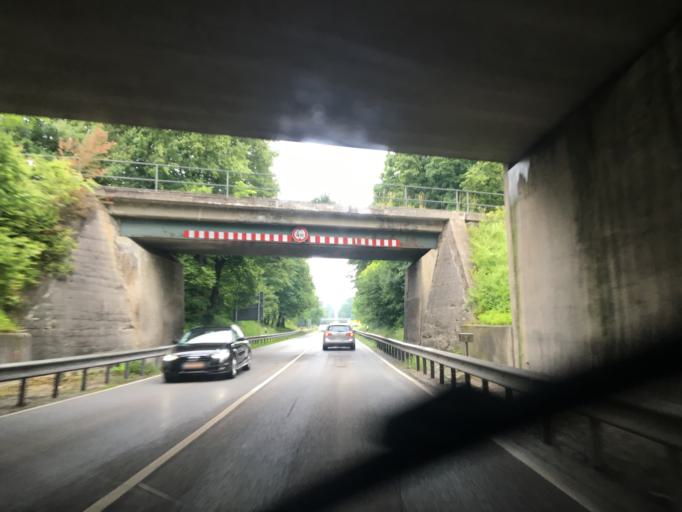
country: DE
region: Bavaria
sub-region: Upper Bavaria
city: Holzkirchen
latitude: 47.8763
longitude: 11.7186
